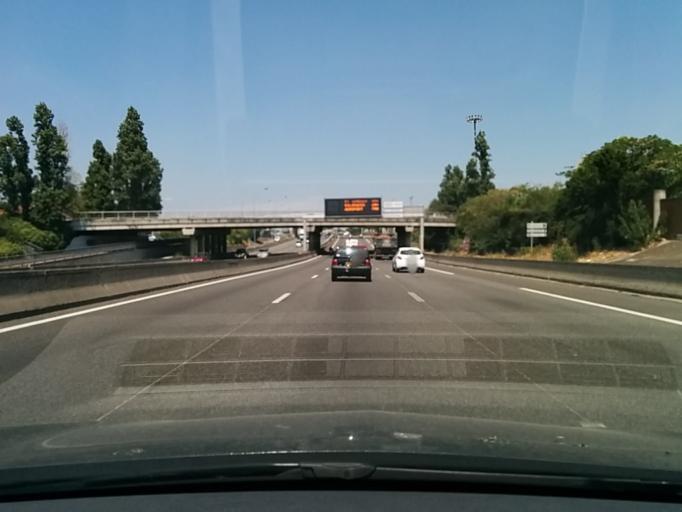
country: FR
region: Midi-Pyrenees
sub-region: Departement de la Haute-Garonne
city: Toulouse
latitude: 43.5760
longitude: 1.4084
